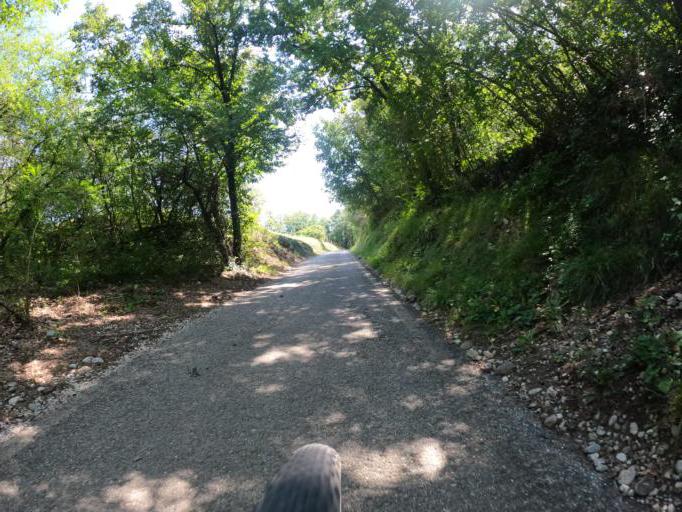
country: IT
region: Veneto
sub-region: Provincia di Verona
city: Rivoli Veronese
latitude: 45.5617
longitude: 10.8155
